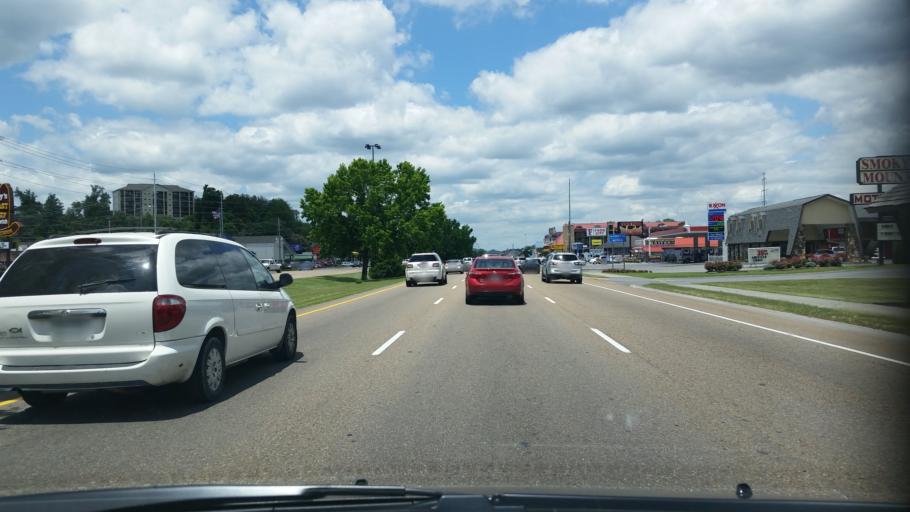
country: US
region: Tennessee
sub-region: Sevier County
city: Pigeon Forge
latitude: 35.7820
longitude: -83.5499
